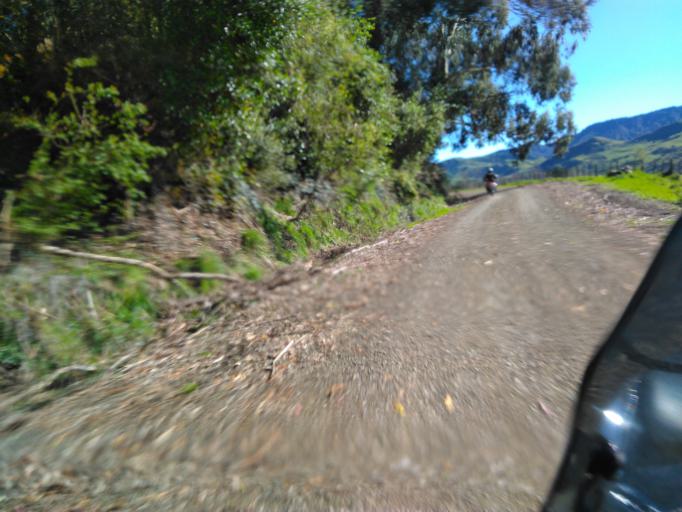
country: NZ
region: Bay of Plenty
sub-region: Opotiki District
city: Opotiki
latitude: -38.3721
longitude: 177.6032
